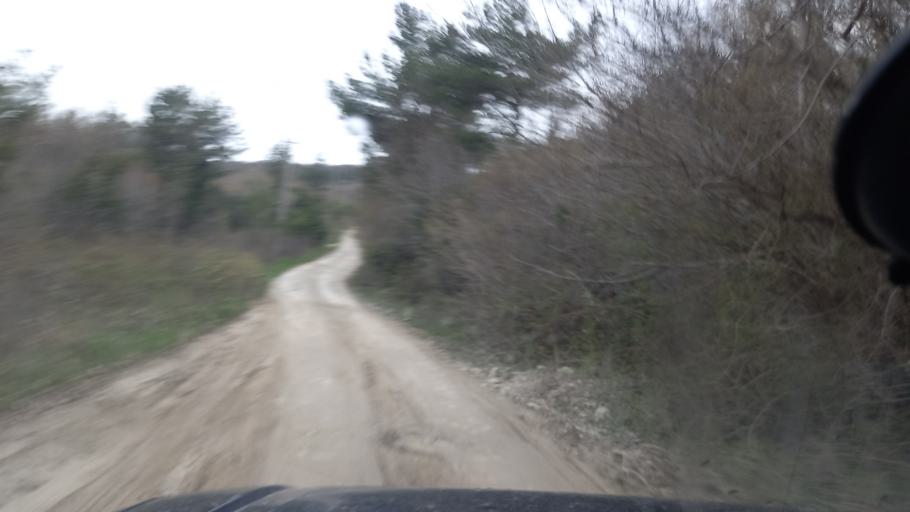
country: RU
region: Krasnodarskiy
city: Dzhubga
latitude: 44.3230
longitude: 38.6871
